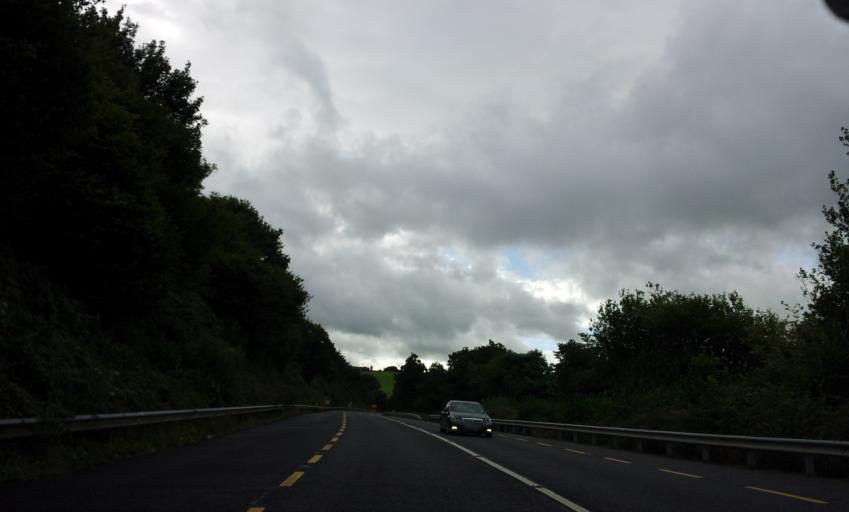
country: IE
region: Leinster
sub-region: Kilkenny
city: Mooncoin
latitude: 52.2382
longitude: -7.2824
